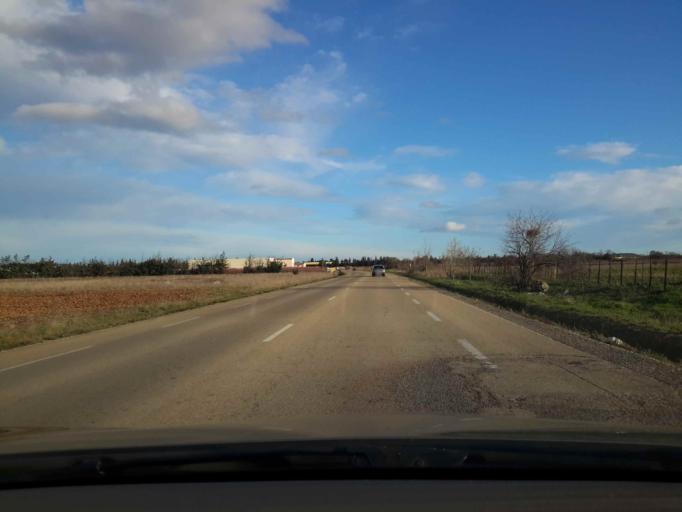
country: FR
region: Languedoc-Roussillon
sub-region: Departement du Gard
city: Aubord
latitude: 43.7631
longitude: 4.3332
